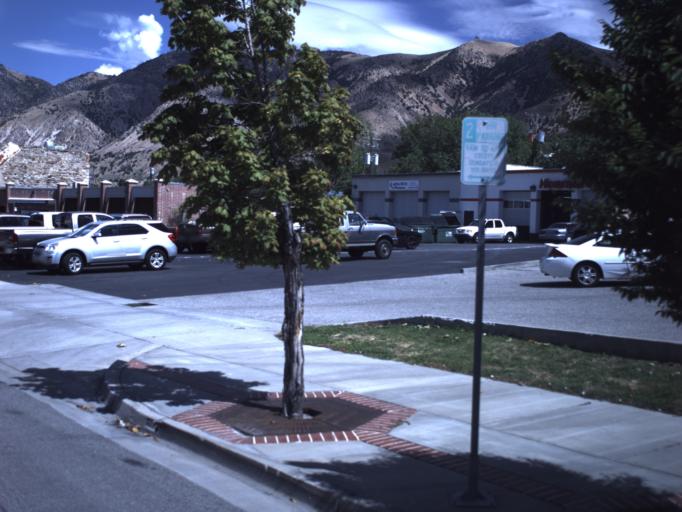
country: US
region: Utah
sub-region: Box Elder County
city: Brigham City
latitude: 41.5064
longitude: -112.0158
